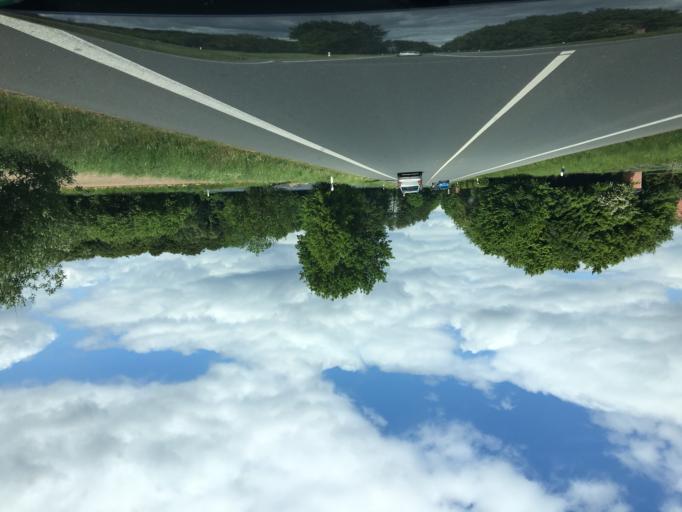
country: DE
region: North Rhine-Westphalia
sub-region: Regierungsbezirk Munster
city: Muenster
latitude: 52.0128
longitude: 7.6798
